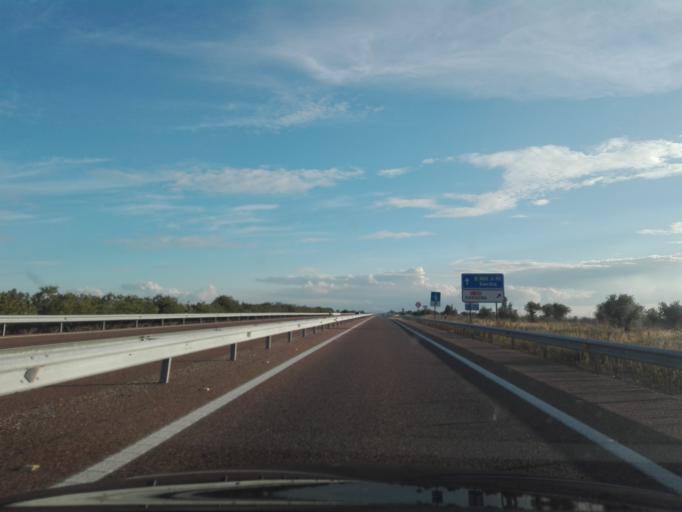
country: ES
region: Extremadura
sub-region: Provincia de Badajoz
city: Puebla de Sancho Perez
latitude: 38.3988
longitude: -6.3406
